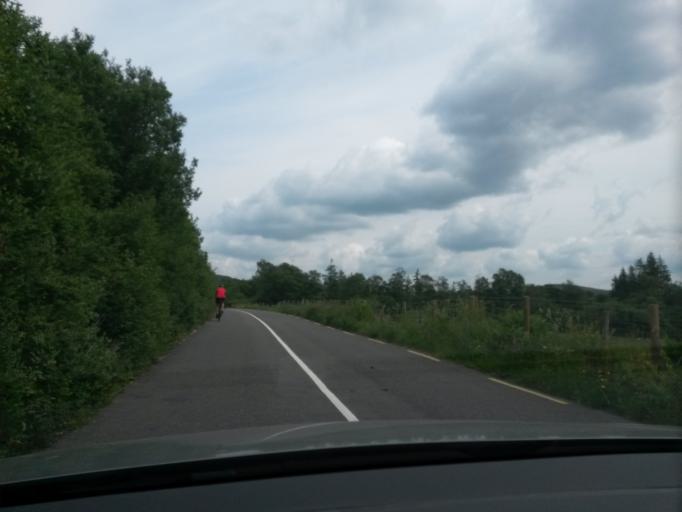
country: IE
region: Munster
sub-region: Ciarrai
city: Kenmare
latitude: 51.9125
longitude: -9.7076
